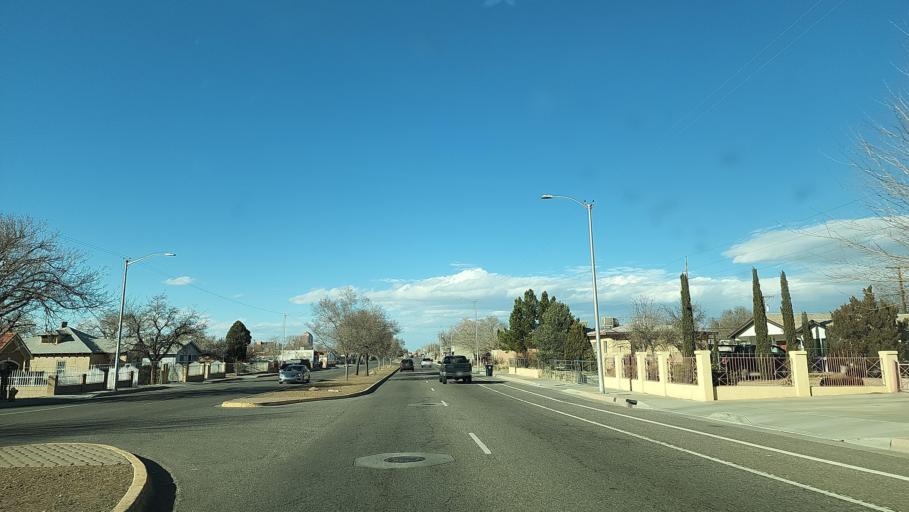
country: US
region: New Mexico
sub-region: Bernalillo County
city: Albuquerque
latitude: 35.0639
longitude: -106.6453
